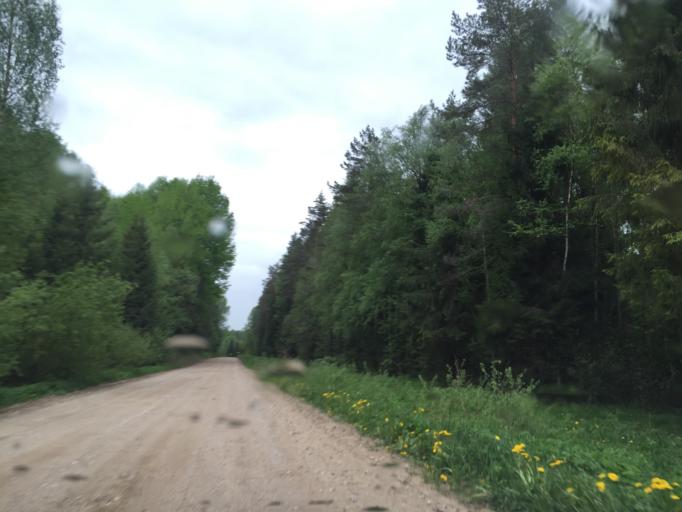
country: LV
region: Ogre
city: Ogre
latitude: 56.8276
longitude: 24.6479
